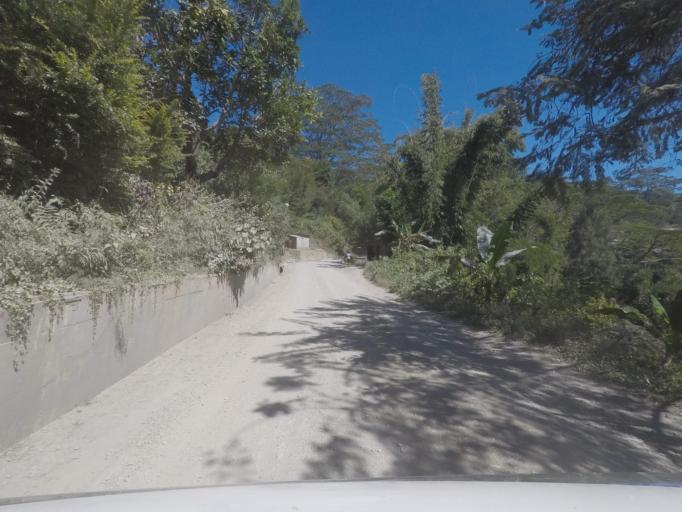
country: TL
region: Ermera
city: Gleno
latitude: -8.7498
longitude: 125.3954
